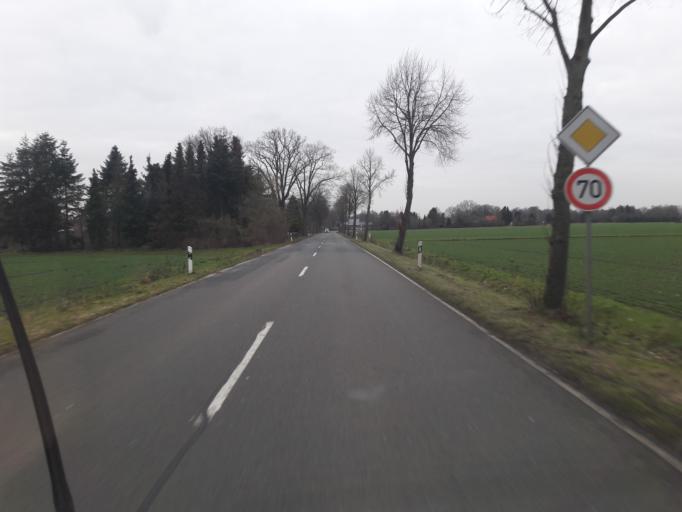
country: DE
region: Lower Saxony
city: Warmsen
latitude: 52.4465
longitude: 8.8551
